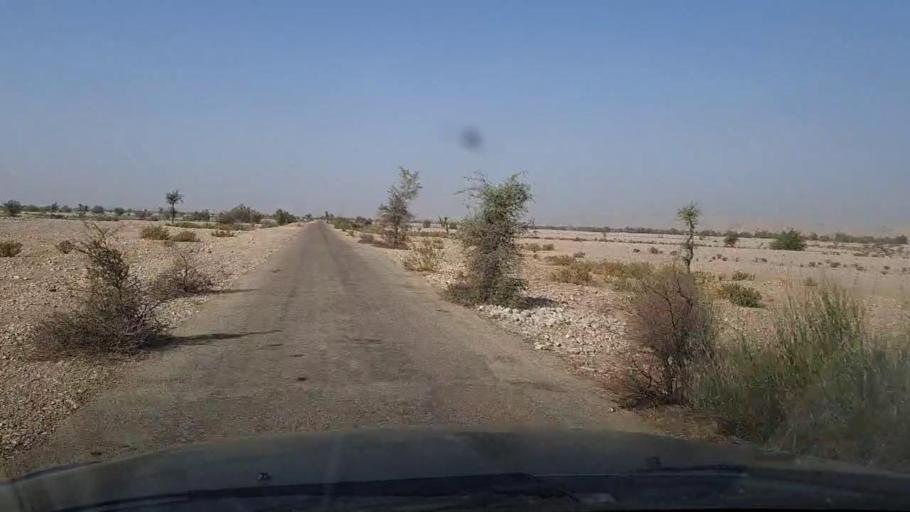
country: PK
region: Sindh
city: Sann
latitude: 25.8943
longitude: 67.9930
